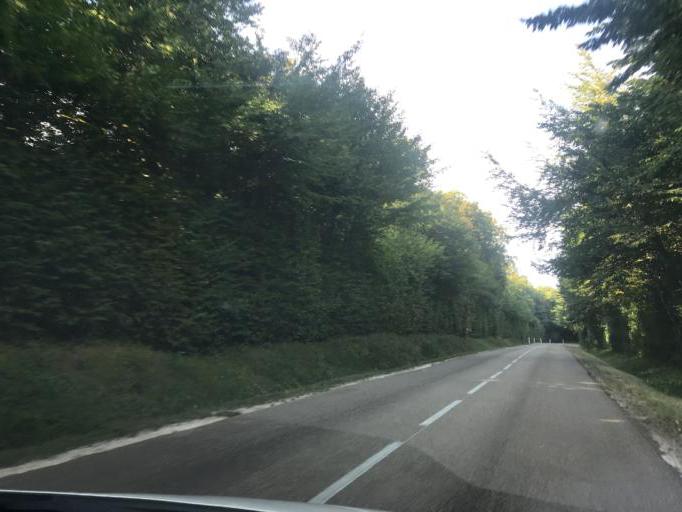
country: FR
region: Bourgogne
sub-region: Departement de l'Yonne
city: Fontenailles
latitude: 47.5759
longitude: 3.4568
